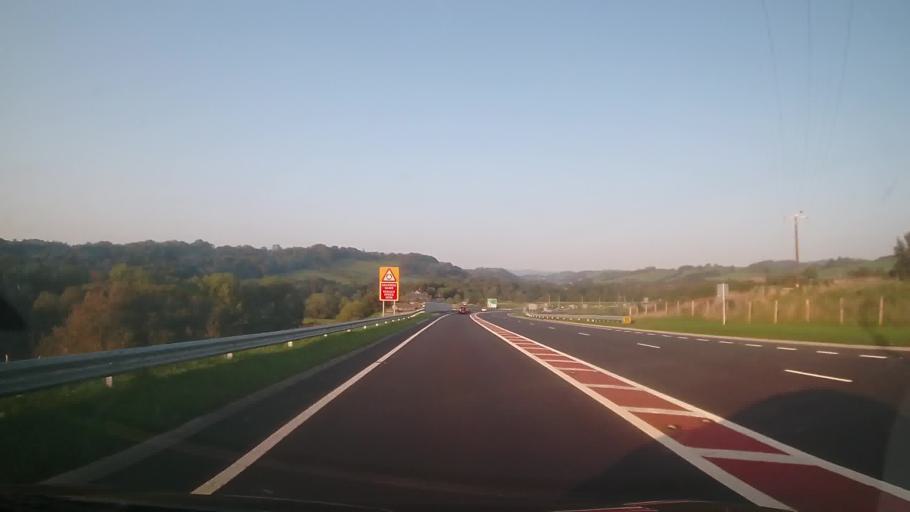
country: GB
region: Wales
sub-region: Sir Powys
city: Newtown
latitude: 52.5184
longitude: -3.2860
